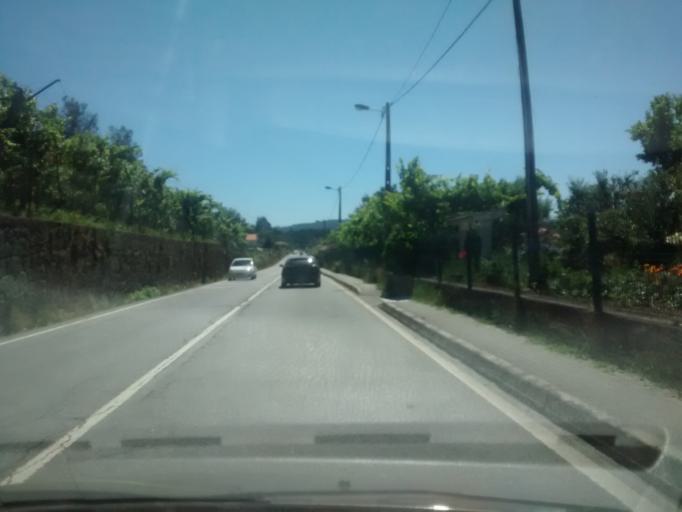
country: PT
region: Braga
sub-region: Barcelos
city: Galegos
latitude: 41.5280
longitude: -8.5611
